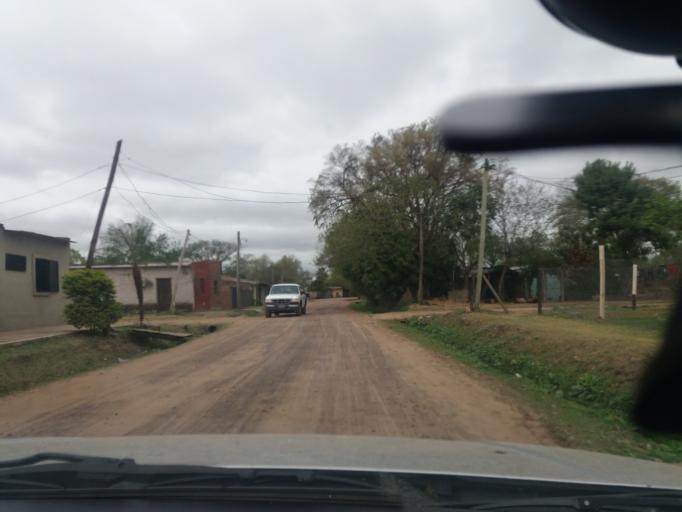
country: AR
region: Corrientes
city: Corrientes
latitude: -27.5108
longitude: -58.8297
